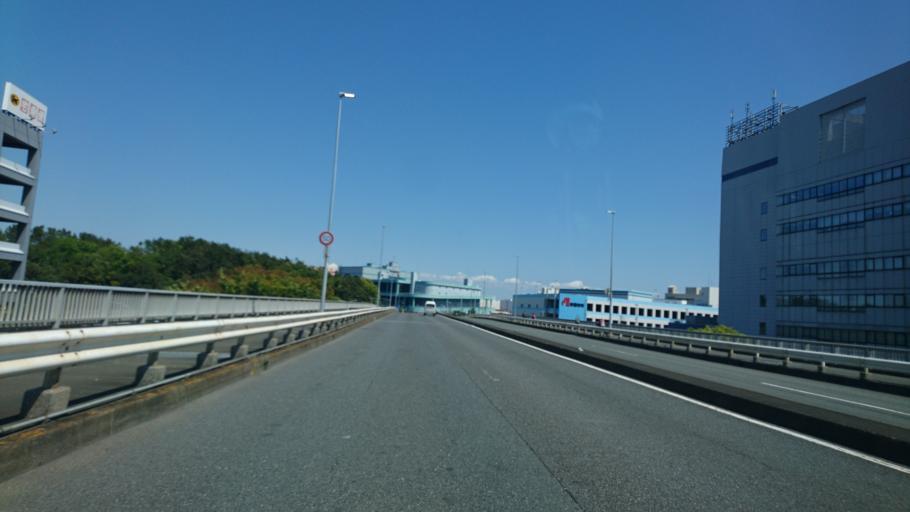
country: JP
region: Kanagawa
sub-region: Kawasaki-shi
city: Kawasaki
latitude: 35.5951
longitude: 139.7604
